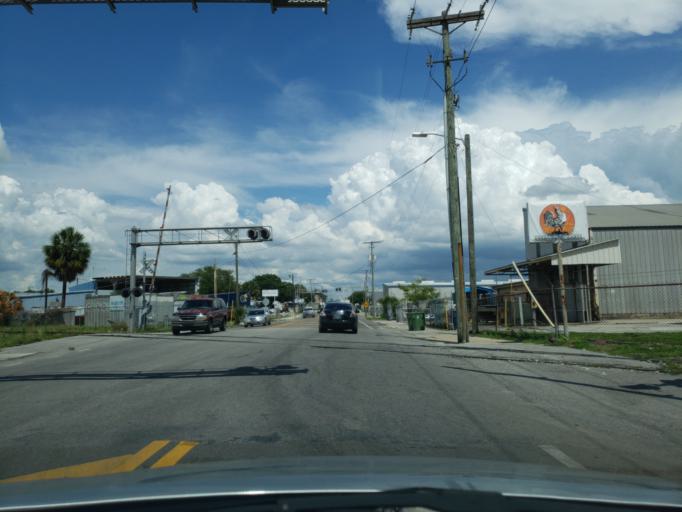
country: US
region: Florida
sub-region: Hillsborough County
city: Tampa
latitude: 27.9602
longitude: -82.4194
